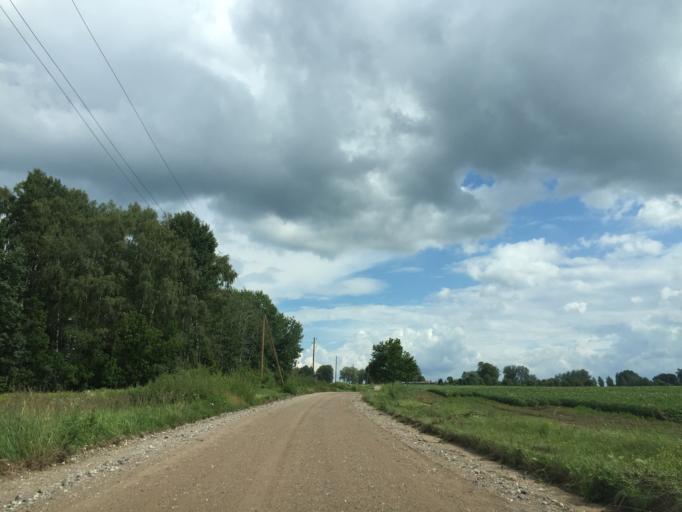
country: LV
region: Ligatne
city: Ligatne
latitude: 57.2142
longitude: 24.9518
